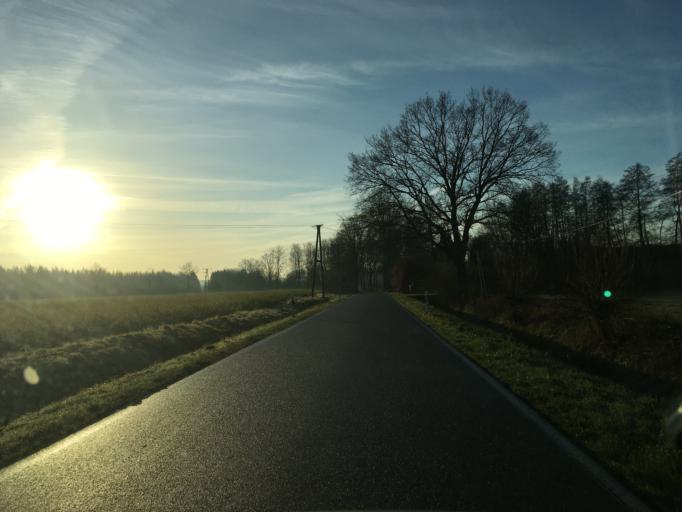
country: DE
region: North Rhine-Westphalia
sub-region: Regierungsbezirk Munster
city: Horstmar
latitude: 52.0585
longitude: 7.2669
